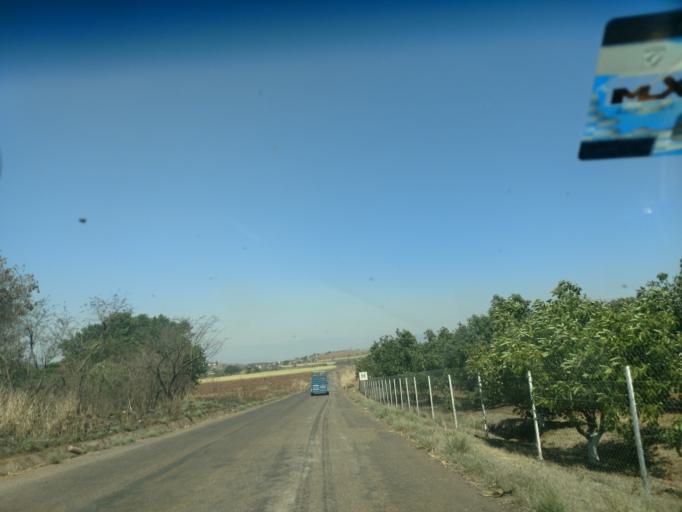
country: MX
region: Nayarit
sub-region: Tepic
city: La Corregidora
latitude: 21.5040
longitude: -104.7259
